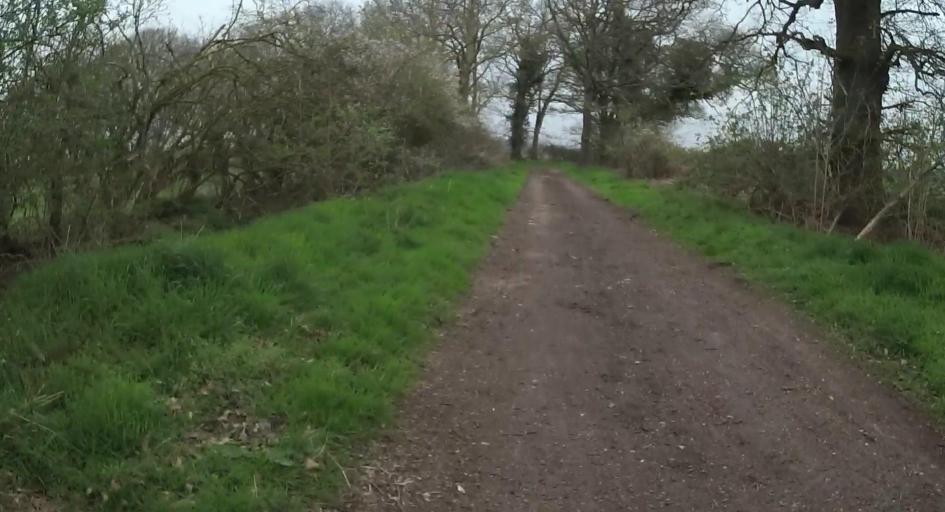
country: GB
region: England
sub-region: West Berkshire
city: Arborfield
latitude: 51.4089
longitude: -0.9081
